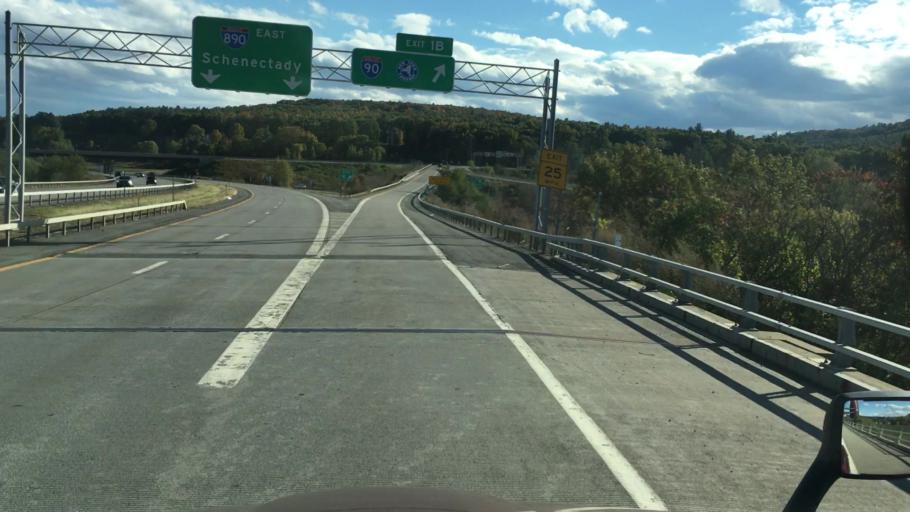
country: US
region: New York
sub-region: Schenectady County
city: Scotia
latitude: 42.8452
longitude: -74.0066
